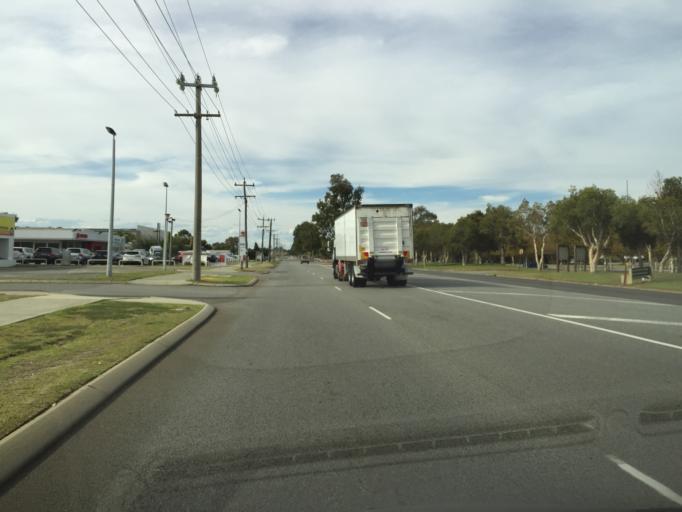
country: AU
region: Western Australia
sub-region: Canning
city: Willetton
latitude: -32.0660
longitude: 115.9001
